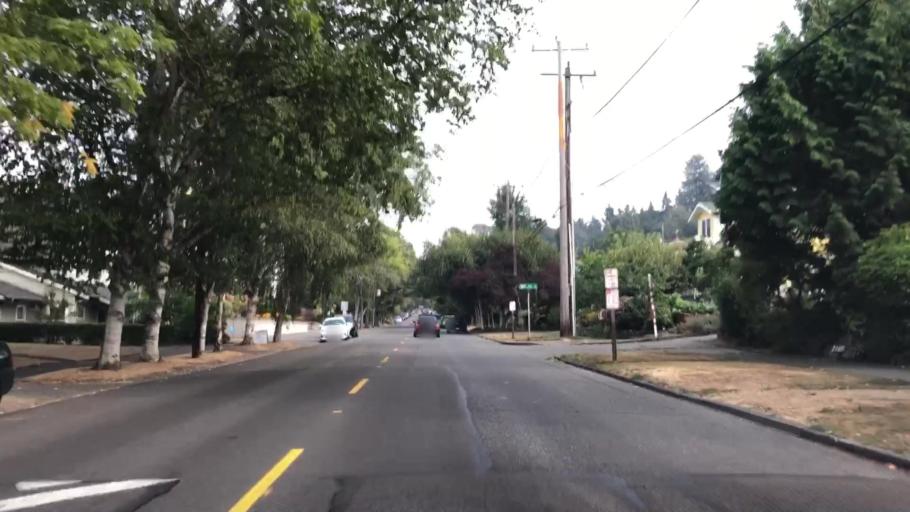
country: US
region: Washington
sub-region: King County
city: Seattle
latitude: 47.6388
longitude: -122.3091
